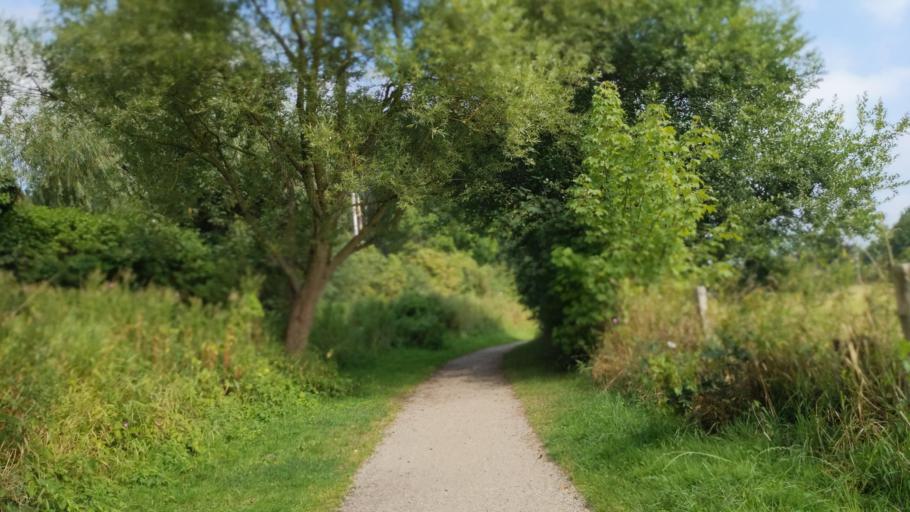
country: DE
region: Schleswig-Holstein
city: Stockelsdorf
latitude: 53.8815
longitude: 10.6321
